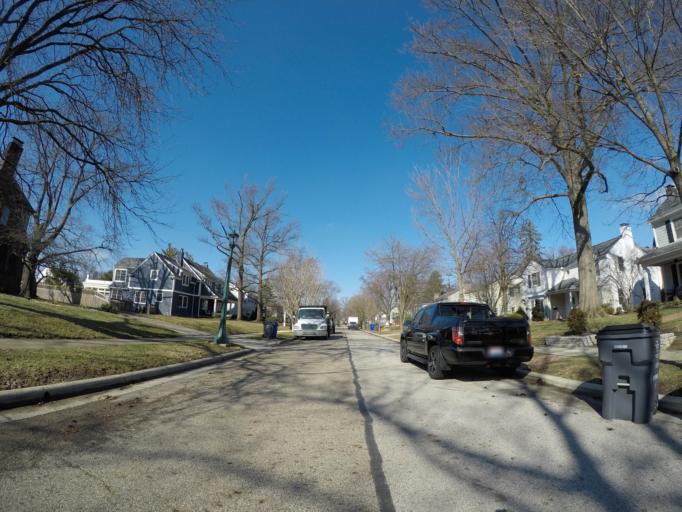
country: US
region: Ohio
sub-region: Franklin County
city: Upper Arlington
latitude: 40.0034
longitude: -83.0530
